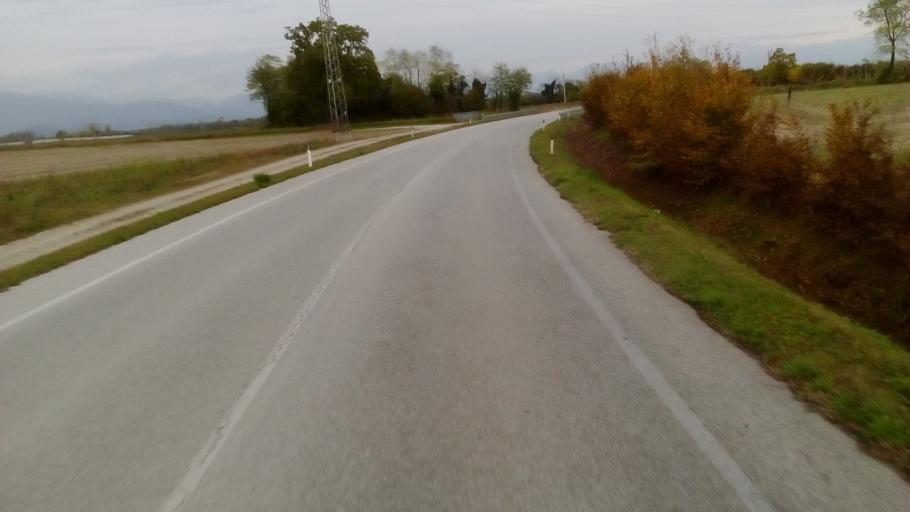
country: IT
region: Friuli Venezia Giulia
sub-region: Provincia di Pordenone
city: Vivaro
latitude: 46.0921
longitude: 12.7820
